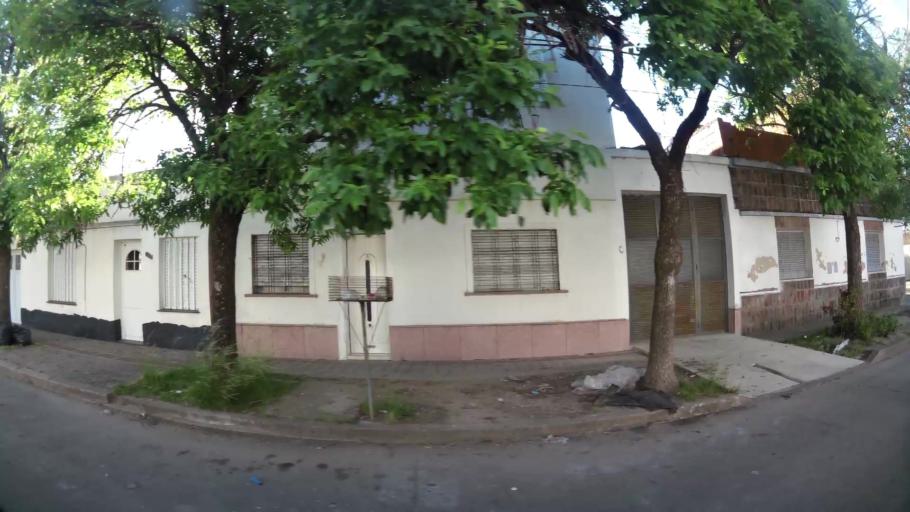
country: AR
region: Cordoba
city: San Francisco
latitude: -31.4401
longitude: -62.0918
